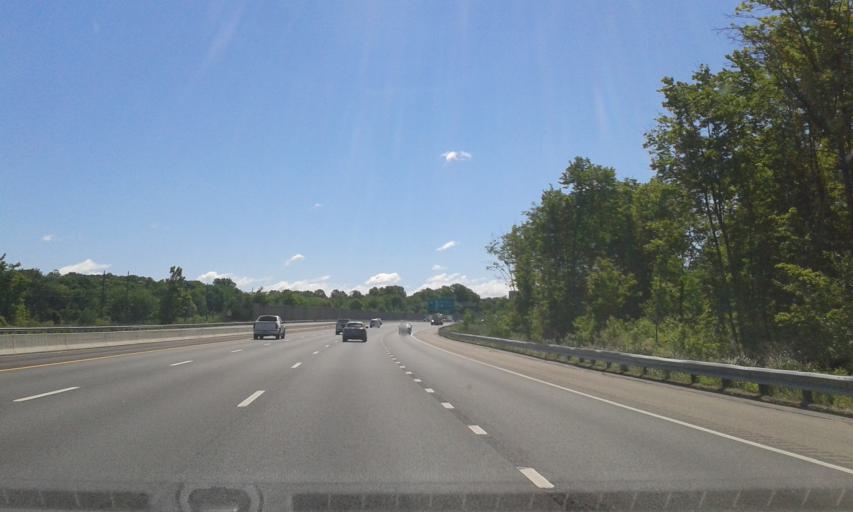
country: US
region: Massachusetts
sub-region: Middlesex County
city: Lowell
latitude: 42.6206
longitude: -71.3425
